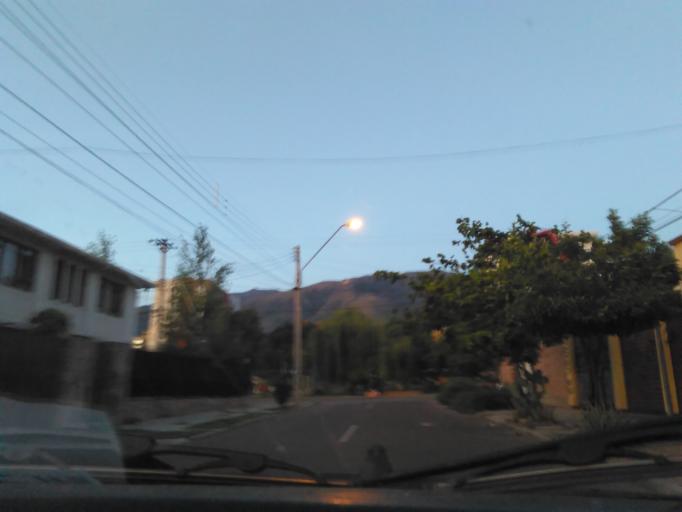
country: BO
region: Cochabamba
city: Cochabamba
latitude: -17.3711
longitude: -66.1657
